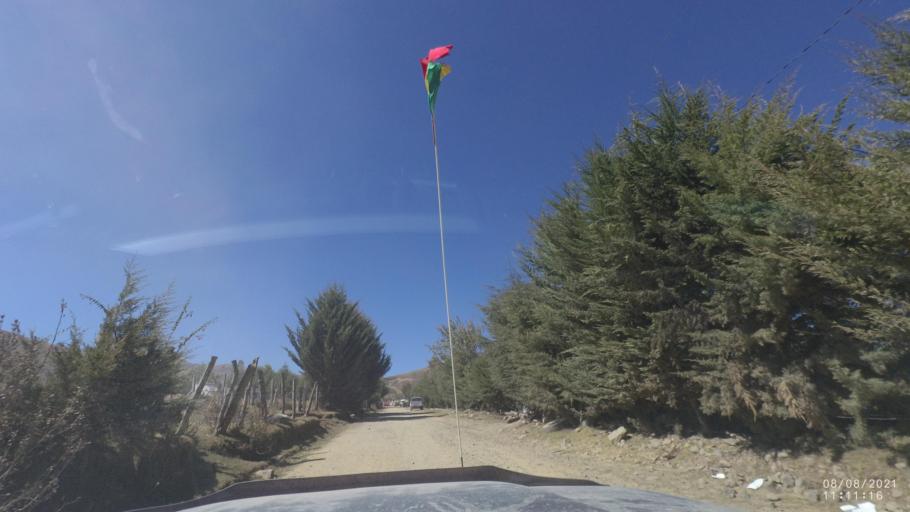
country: BO
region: Cochabamba
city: Colchani
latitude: -16.7614
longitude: -66.6686
